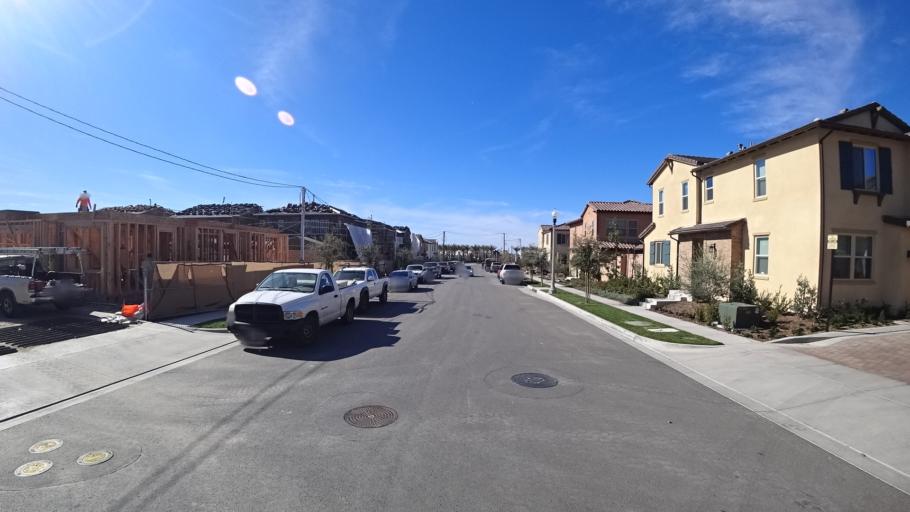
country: US
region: California
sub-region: Orange County
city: Foothill Ranch
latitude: 33.6787
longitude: -117.6809
